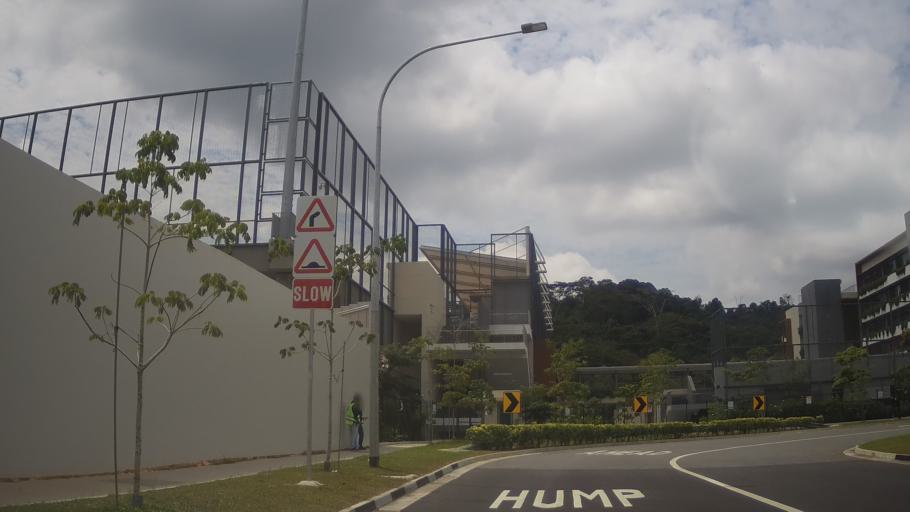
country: MY
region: Johor
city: Johor Bahru
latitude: 1.3664
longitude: 103.7738
